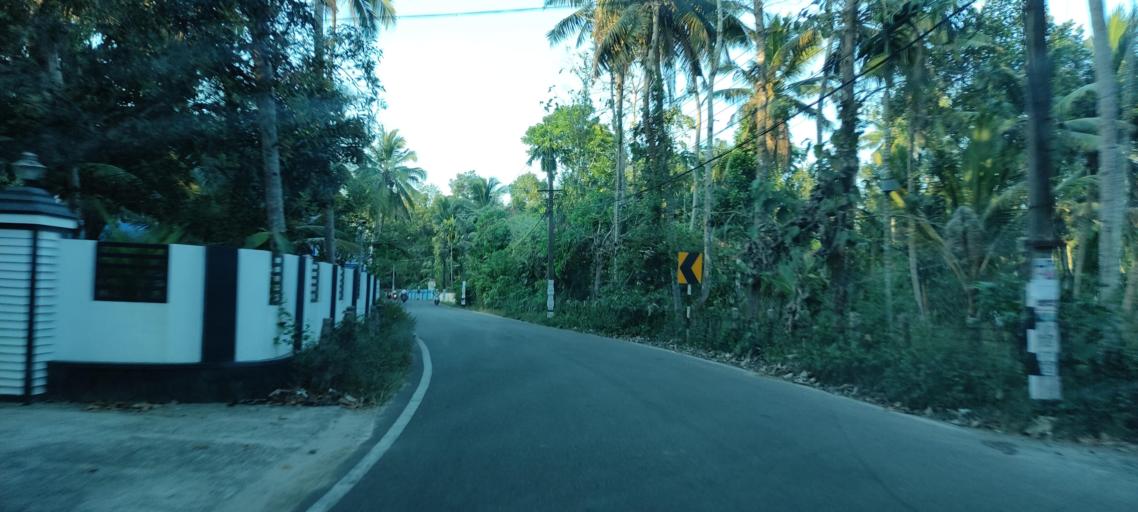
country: IN
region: Kerala
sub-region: Alappuzha
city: Kayankulam
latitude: 9.1999
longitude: 76.4646
